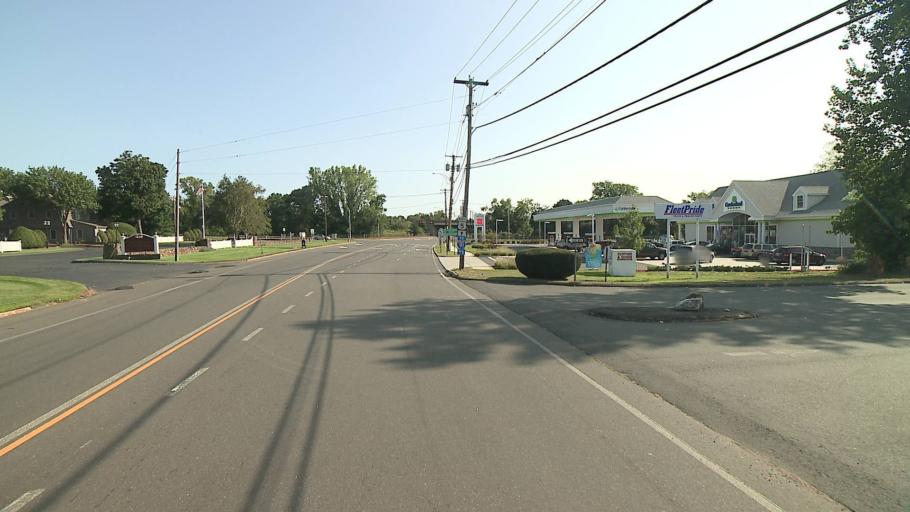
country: US
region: Connecticut
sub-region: New Haven County
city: Hamden
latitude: 41.3767
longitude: -72.8829
